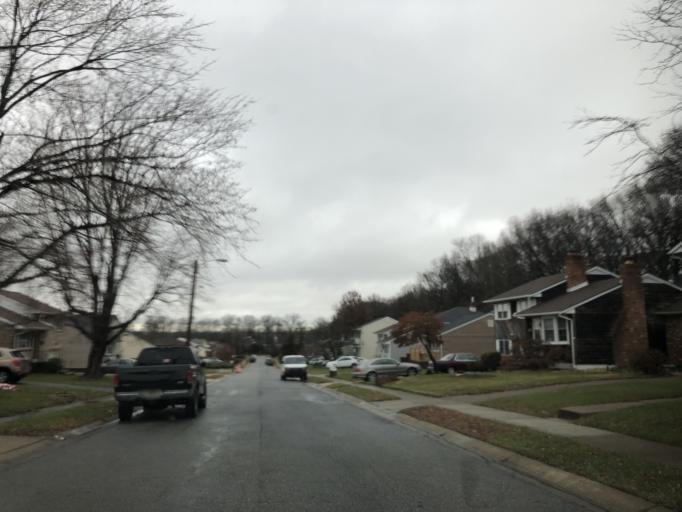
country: US
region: Delaware
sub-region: New Castle County
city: Wilmington Manor
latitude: 39.7093
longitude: -75.5604
